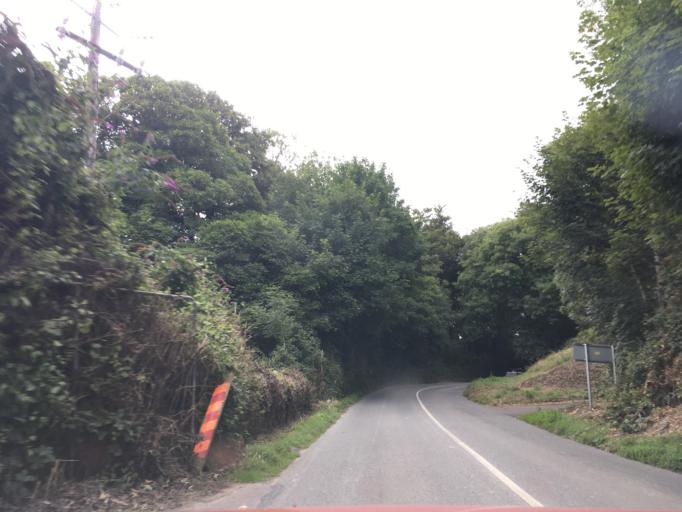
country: IE
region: Munster
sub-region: County Cork
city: Crosshaven
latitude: 51.7984
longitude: -8.2967
